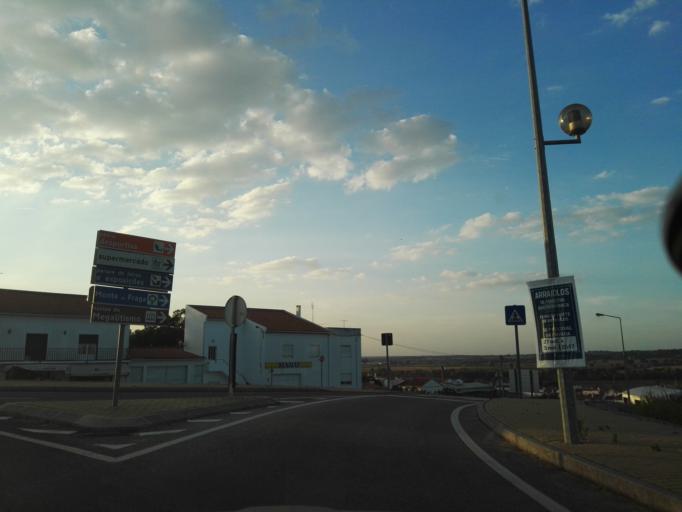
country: PT
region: Evora
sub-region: Mora
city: Mora
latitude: 38.9437
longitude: -8.1568
